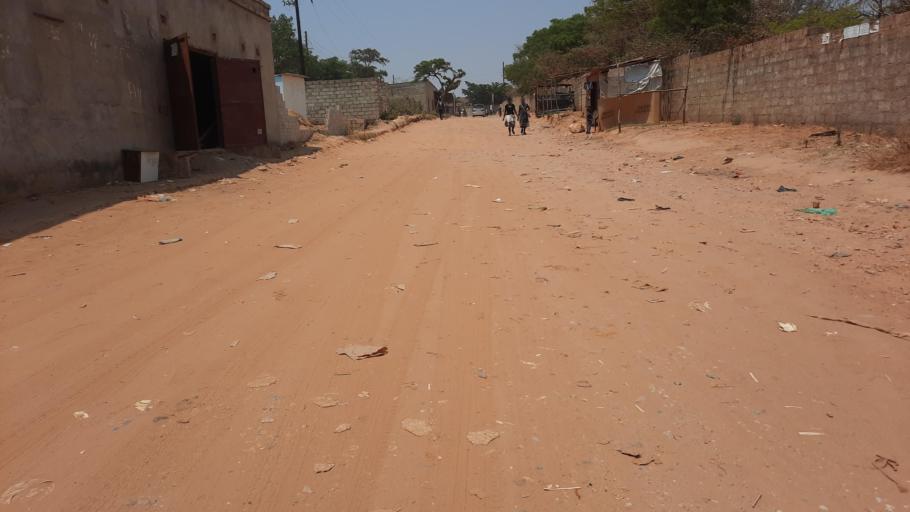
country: ZM
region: Lusaka
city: Lusaka
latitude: -15.4093
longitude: 28.3797
